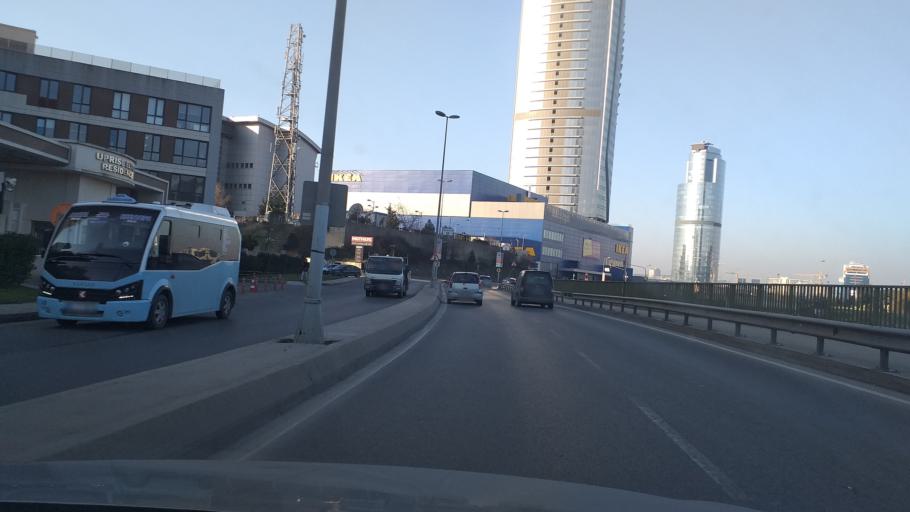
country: TR
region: Istanbul
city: Maltepe
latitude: 40.9200
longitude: 29.1786
